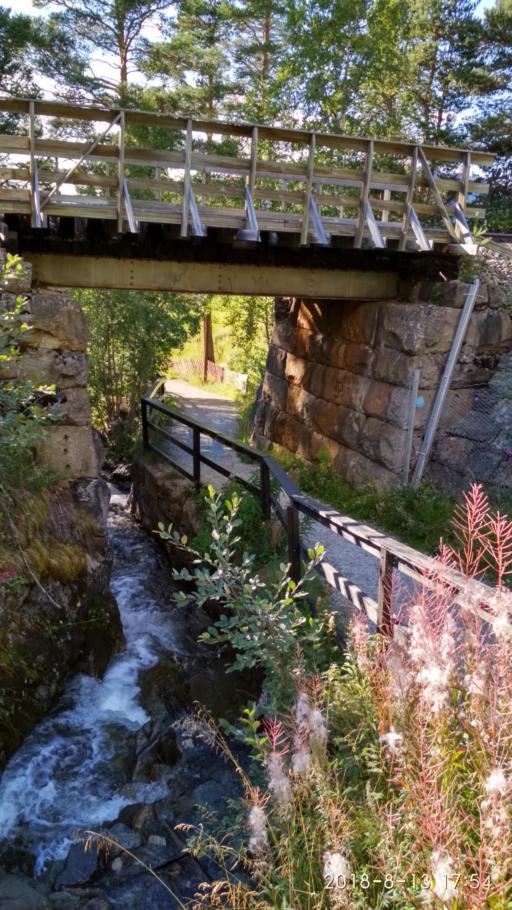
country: NO
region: Oppland
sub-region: Dovre
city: Dombas
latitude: 62.0771
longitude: 9.1313
